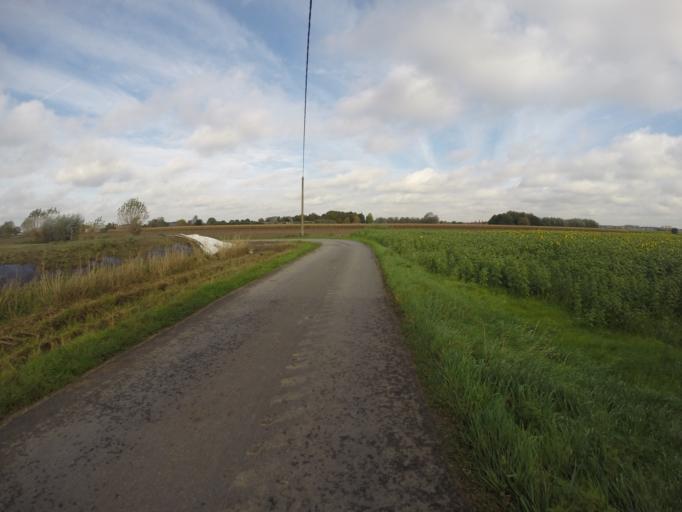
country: BE
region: Flanders
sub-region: Provincie Oost-Vlaanderen
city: Knesselare
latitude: 51.1129
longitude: 3.4157
